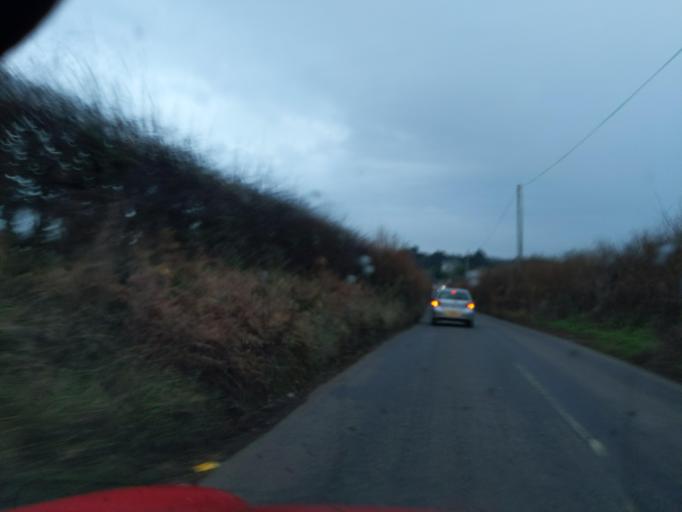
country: GB
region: England
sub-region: Devon
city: Wembury
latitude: 50.3433
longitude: -4.0755
